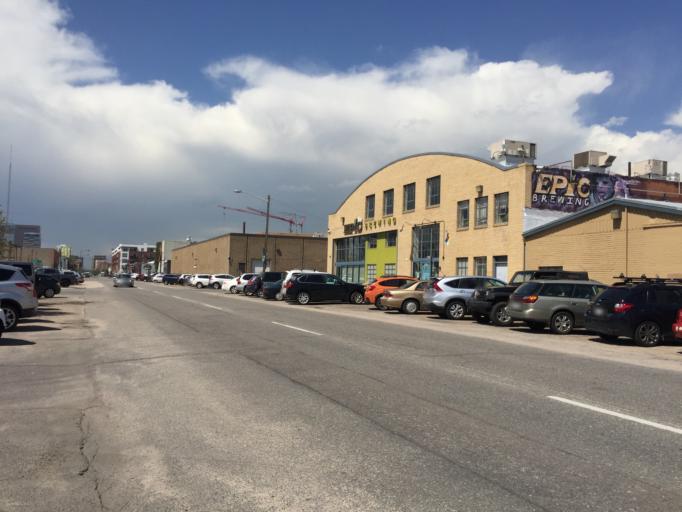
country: US
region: Colorado
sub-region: Denver County
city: Denver
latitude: 39.7633
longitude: -104.9811
